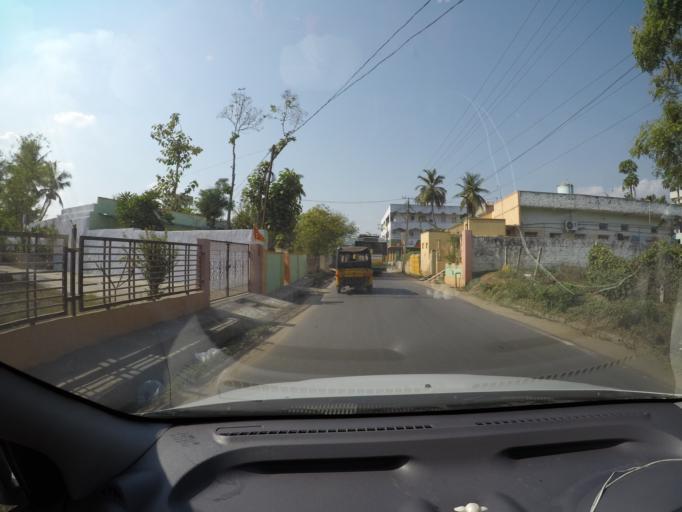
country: IN
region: Andhra Pradesh
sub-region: Krishna
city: Kankipadu
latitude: 16.4363
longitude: 80.7687
